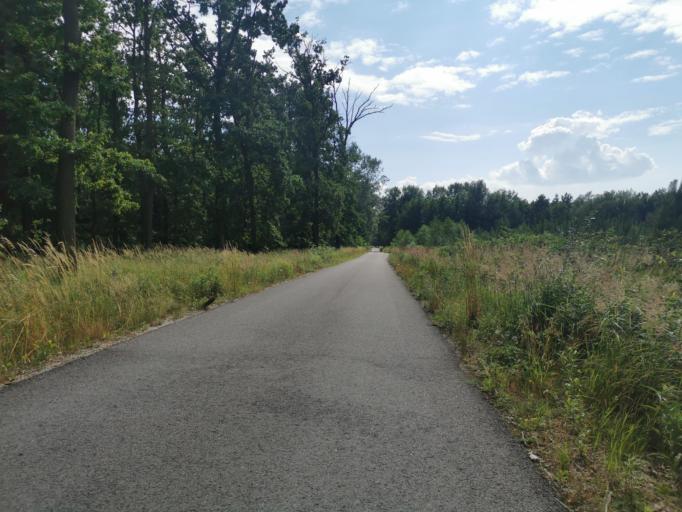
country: SK
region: Trnavsky
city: Gbely
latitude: 48.7304
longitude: 17.0921
